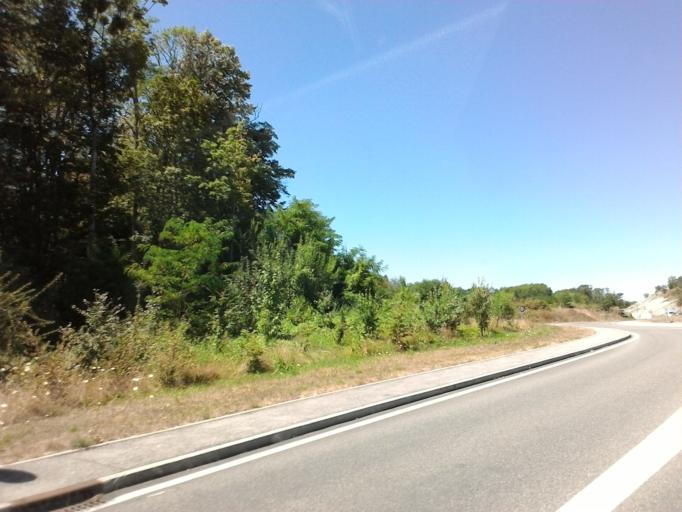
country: FR
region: Franche-Comte
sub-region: Departement du Jura
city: Montmorot
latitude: 46.6605
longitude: 5.5074
